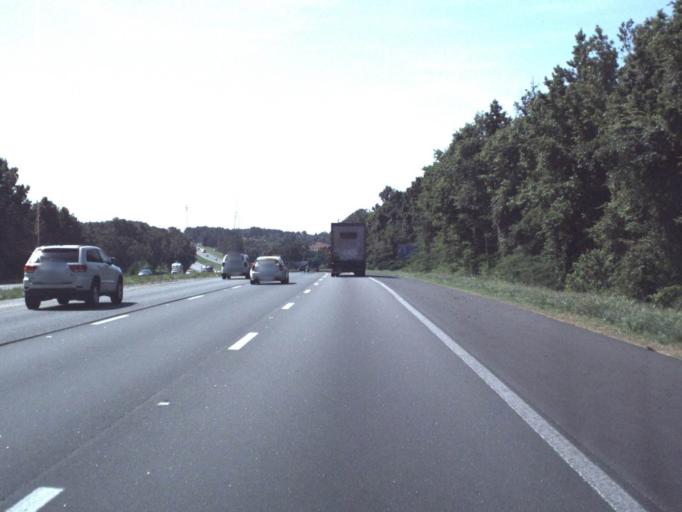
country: US
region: Florida
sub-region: Alachua County
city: Alachua
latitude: 29.7027
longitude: -82.4588
